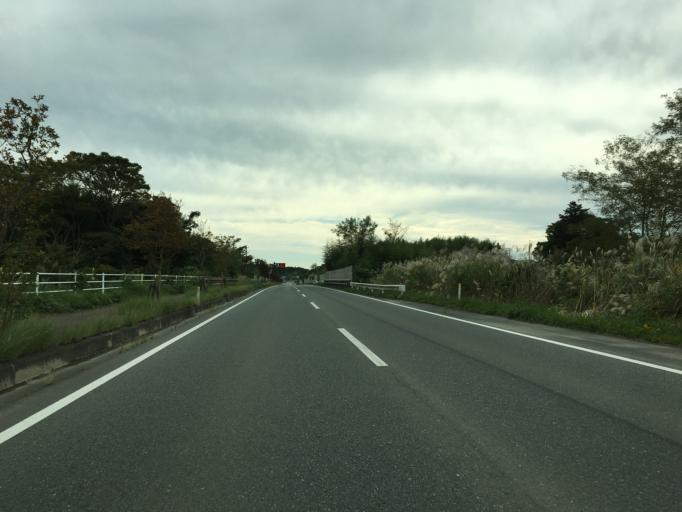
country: JP
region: Miyagi
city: Marumori
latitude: 37.8260
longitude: 140.9408
